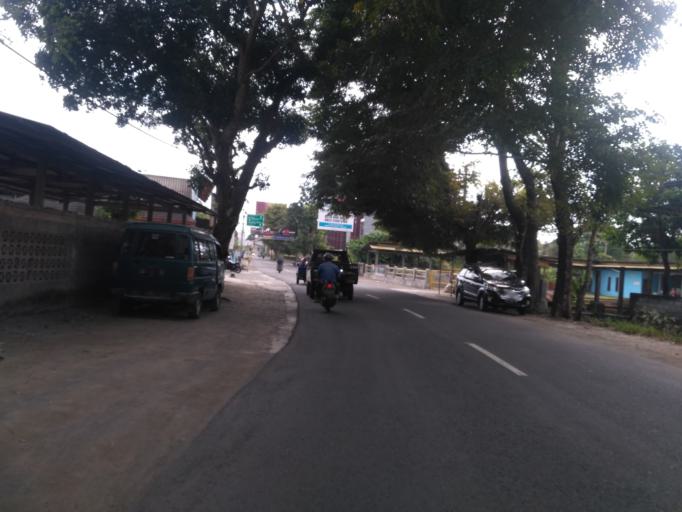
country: ID
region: Daerah Istimewa Yogyakarta
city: Melati
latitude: -7.7389
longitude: 110.3550
